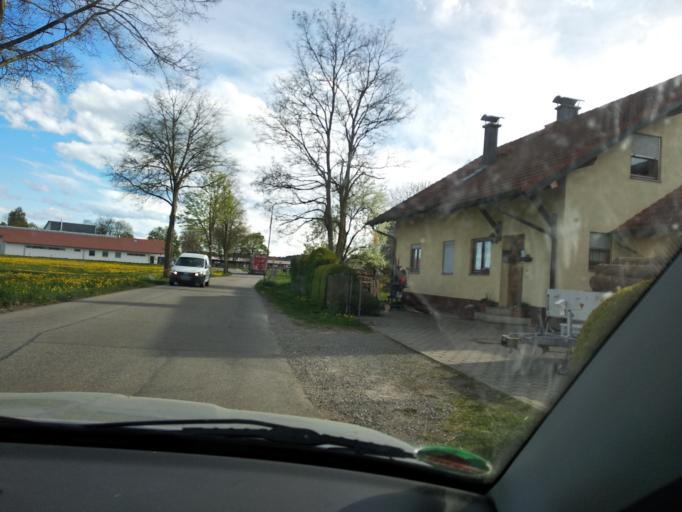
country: DE
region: Bavaria
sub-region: Swabia
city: Woringen
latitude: 47.9247
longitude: 10.2055
